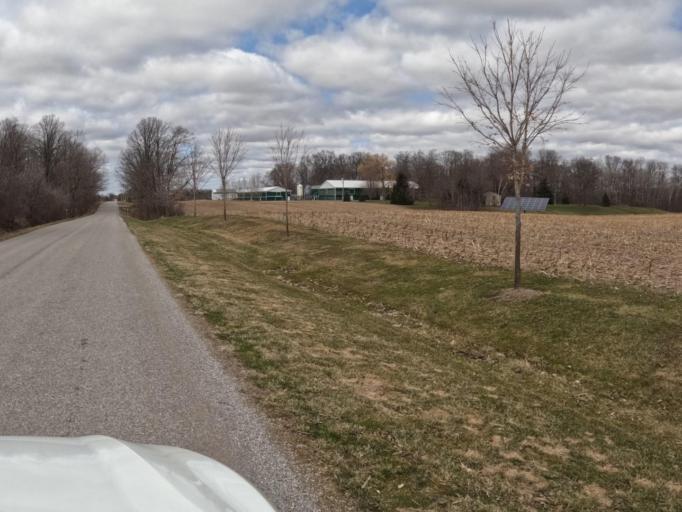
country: CA
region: Ontario
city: Norfolk County
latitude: 42.8472
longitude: -80.1689
